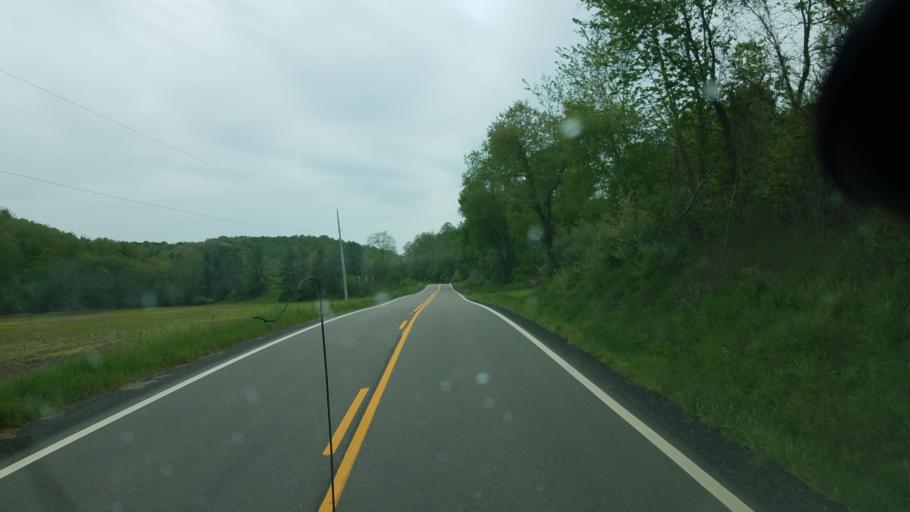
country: US
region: Ohio
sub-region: Coshocton County
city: West Lafayette
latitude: 40.2204
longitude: -81.7850
